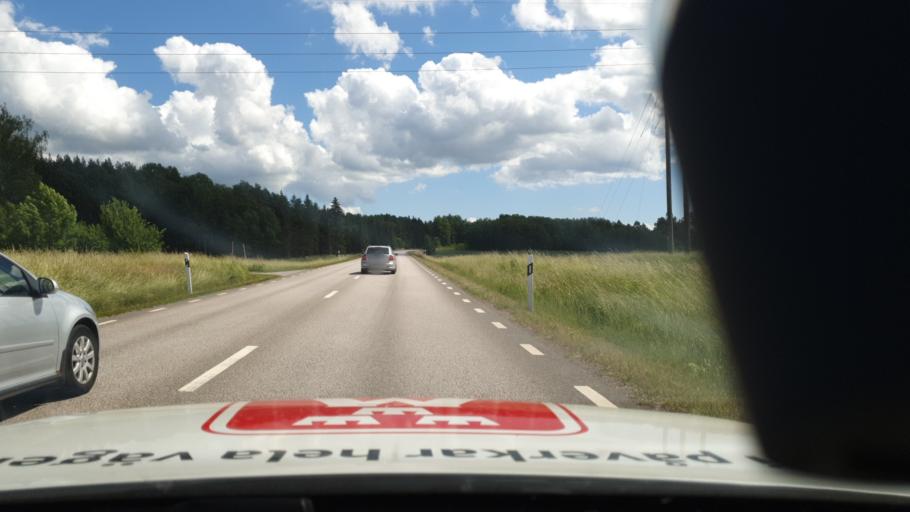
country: SE
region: Vaestra Goetaland
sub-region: Tibro Kommun
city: Tibro
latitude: 58.3486
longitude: 14.1023
